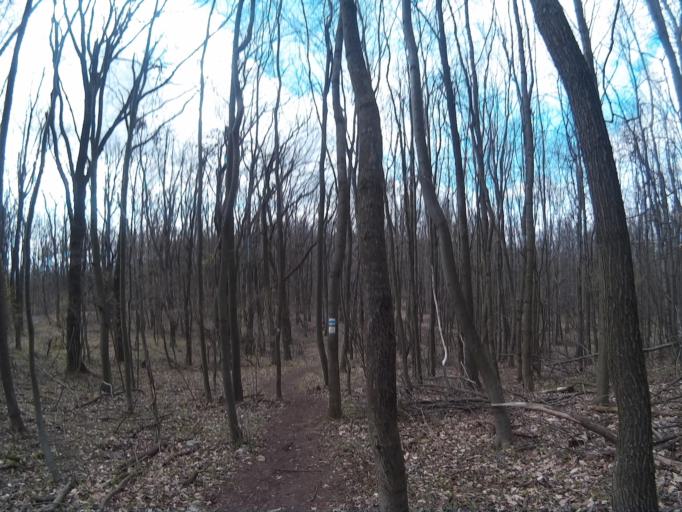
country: HU
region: Pest
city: Kosd
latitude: 47.8344
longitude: 19.1453
